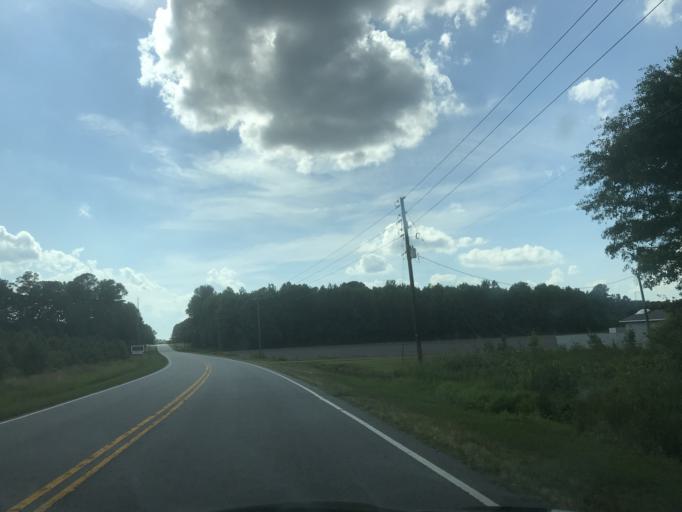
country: US
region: North Carolina
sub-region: Nash County
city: Nashville
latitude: 35.9713
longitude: -78.0018
